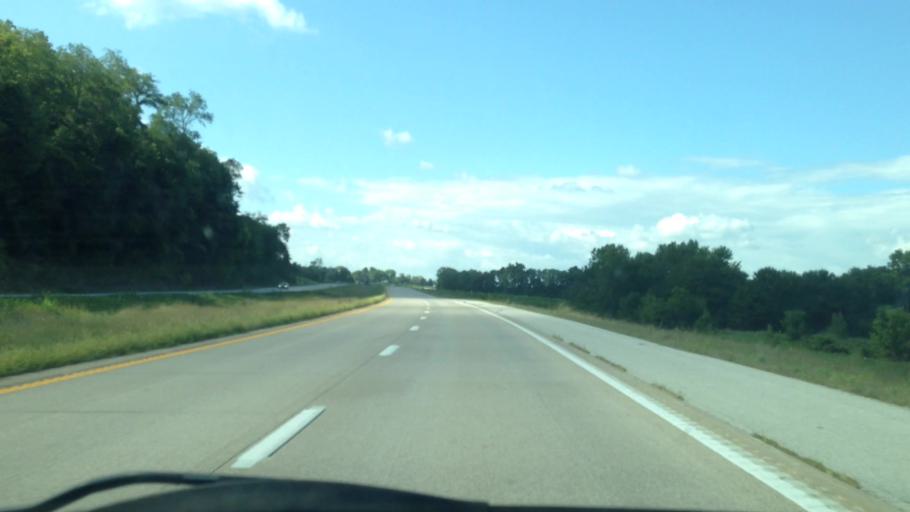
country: US
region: Missouri
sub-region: Lewis County
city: Canton
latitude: 40.2382
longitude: -91.5343
